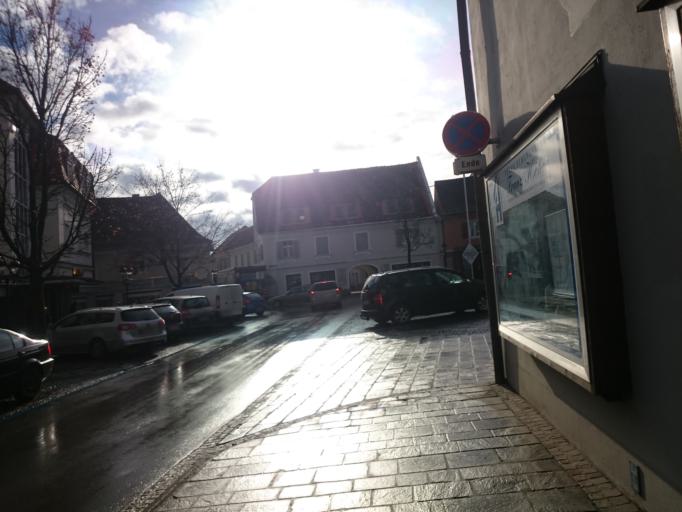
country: AT
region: Styria
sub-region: Politischer Bezirk Weiz
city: Weiz
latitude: 47.2179
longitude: 15.6242
